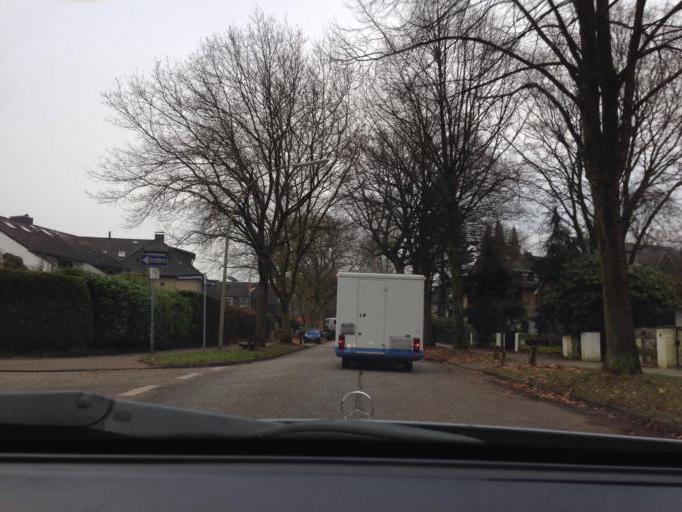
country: DE
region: Schleswig-Holstein
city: Barsbuettel
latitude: 53.5916
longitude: 10.1753
